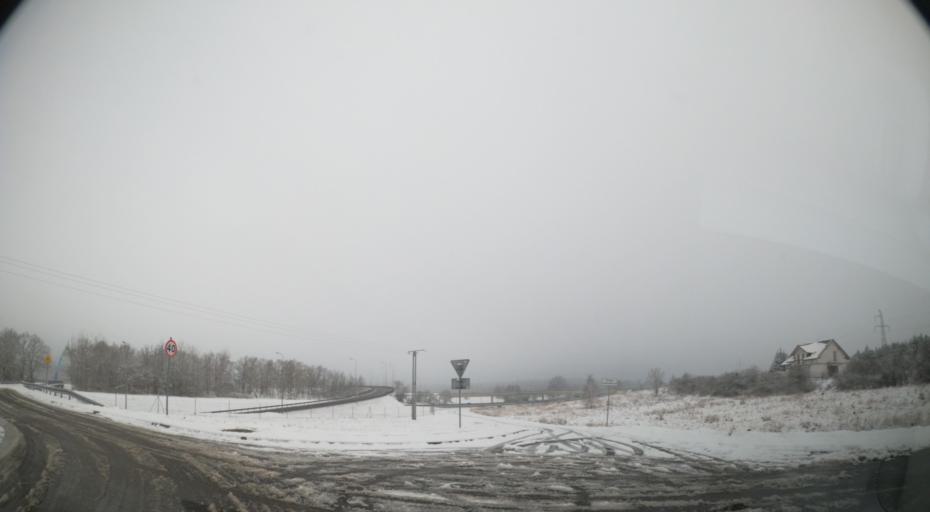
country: PL
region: West Pomeranian Voivodeship
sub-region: Szczecin
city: Szczecin
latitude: 53.3410
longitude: 14.5701
